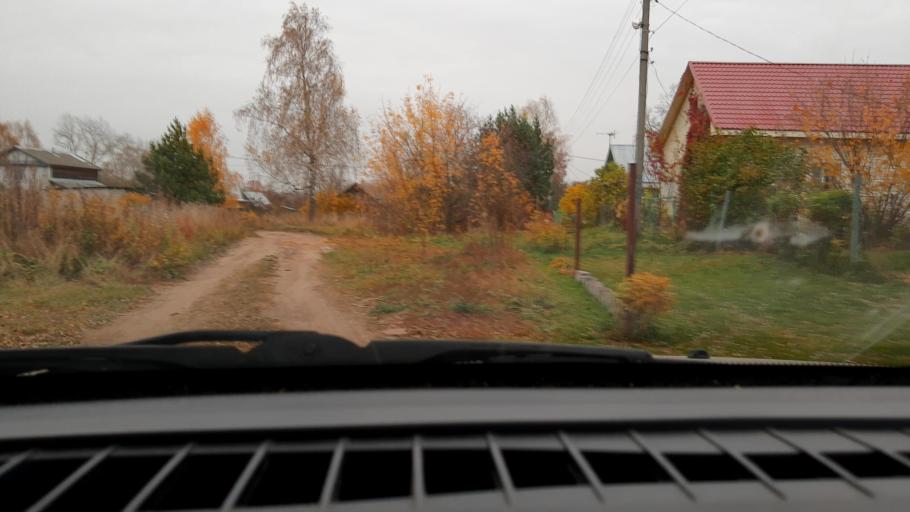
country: RU
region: Nizjnij Novgorod
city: Burevestnik
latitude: 56.0474
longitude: 43.8463
